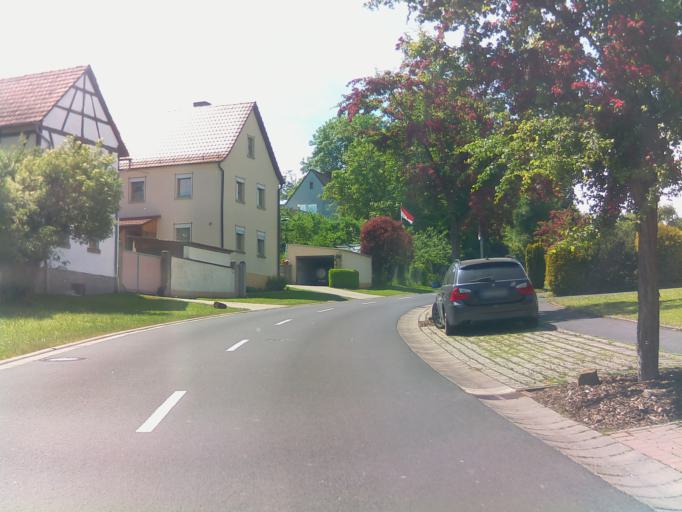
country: DE
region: Bavaria
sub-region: Regierungsbezirk Unterfranken
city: Euerbach
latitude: 50.0751
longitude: 10.0908
